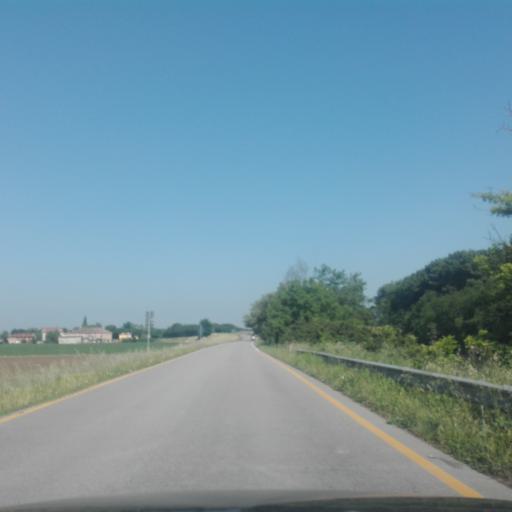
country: IT
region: Veneto
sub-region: Provincia di Rovigo
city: Gavello
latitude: 45.0345
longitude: 11.9186
